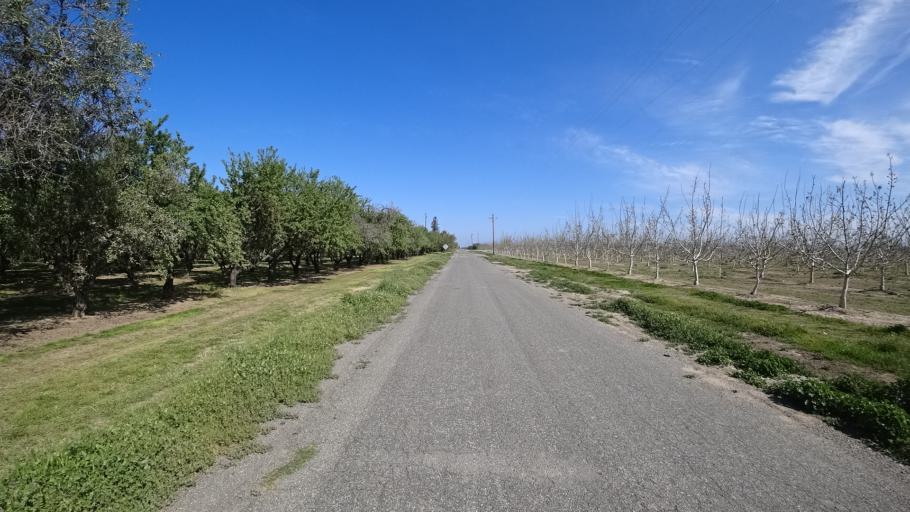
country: US
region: California
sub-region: Glenn County
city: Hamilton City
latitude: 39.6315
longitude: -122.0181
